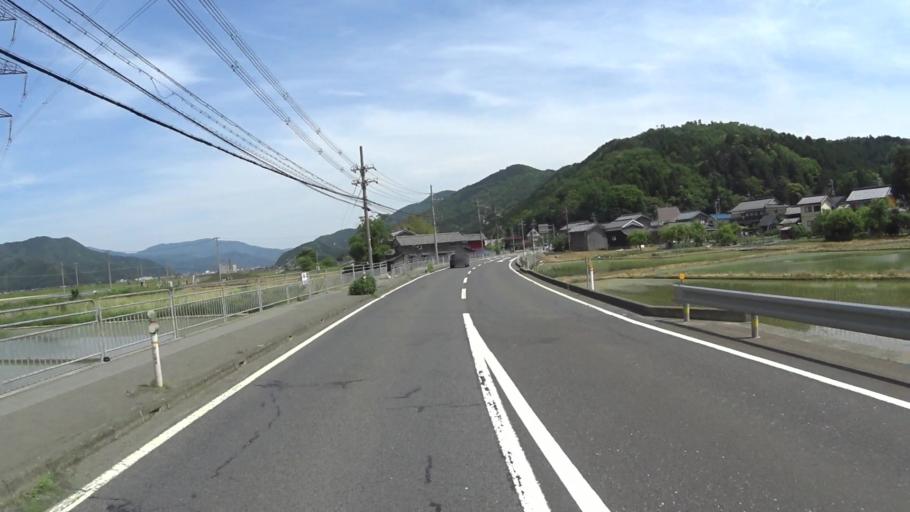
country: JP
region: Fukui
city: Obama
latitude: 35.4784
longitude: 135.7970
